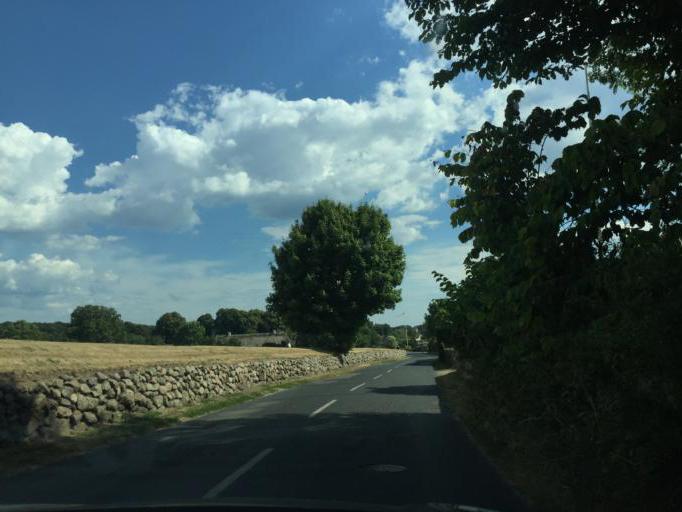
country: DK
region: South Denmark
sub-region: Assens Kommune
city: Harby
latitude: 55.1509
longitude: 10.0180
